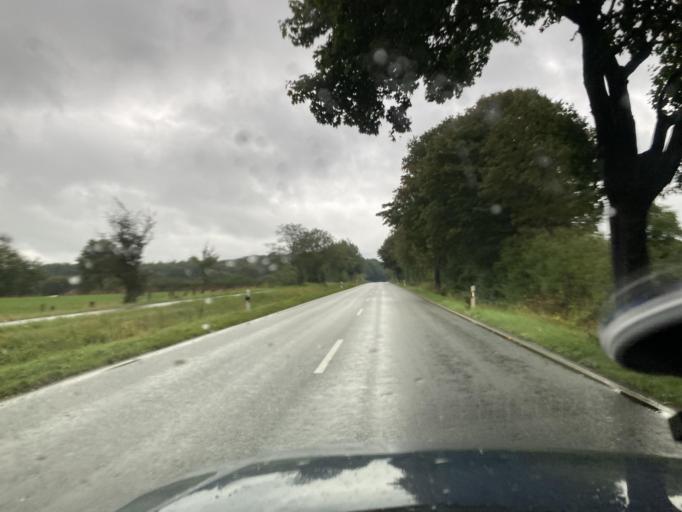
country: DE
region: Schleswig-Holstein
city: Ostrohe
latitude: 54.1963
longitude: 9.1664
